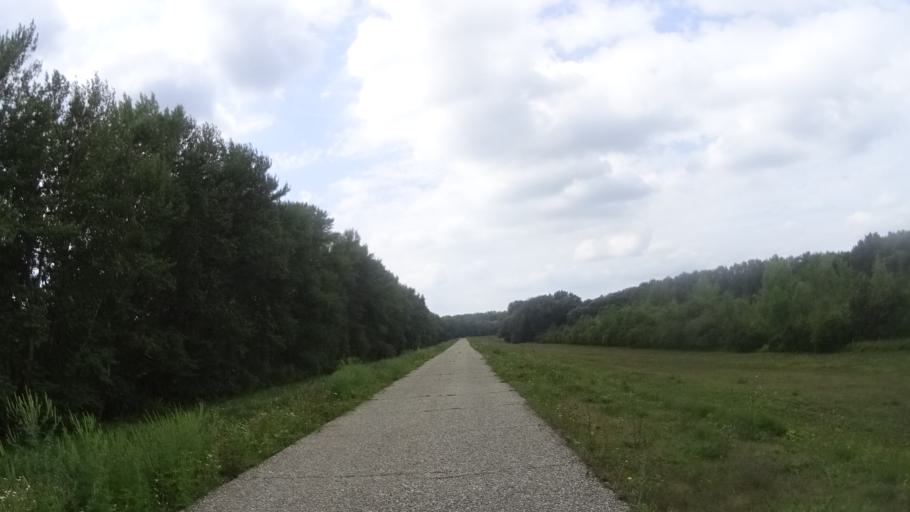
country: SK
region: Trnavsky
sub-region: Okres Dunajska Streda
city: Velky Meder
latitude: 47.7588
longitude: 17.7401
